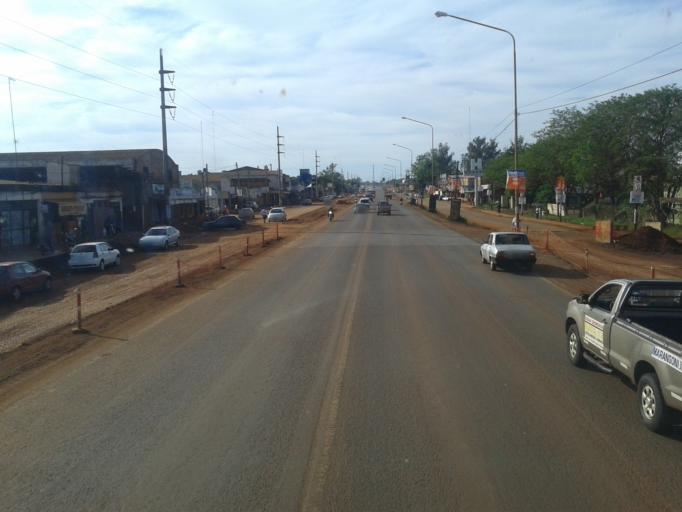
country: AR
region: Misiones
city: Garupa
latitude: -27.4447
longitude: -55.8735
